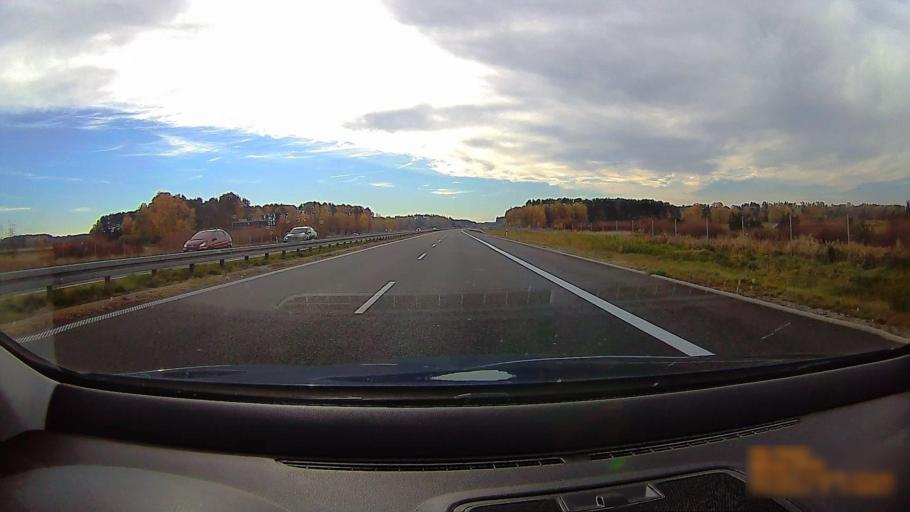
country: PL
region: Greater Poland Voivodeship
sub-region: Powiat ostrowski
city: Przygodzice
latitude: 51.5755
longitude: 17.8490
